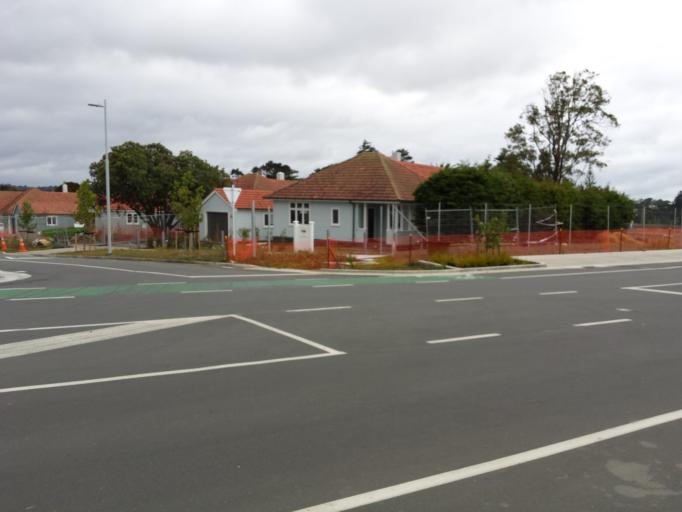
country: NZ
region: Auckland
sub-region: Auckland
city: Rosebank
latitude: -36.7892
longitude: 174.6644
